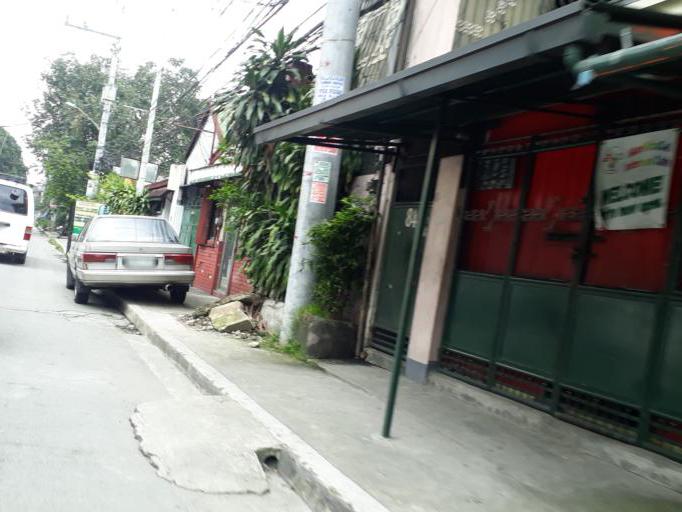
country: PH
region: Calabarzon
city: Bagong Pagasa
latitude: 14.6592
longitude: 121.0346
